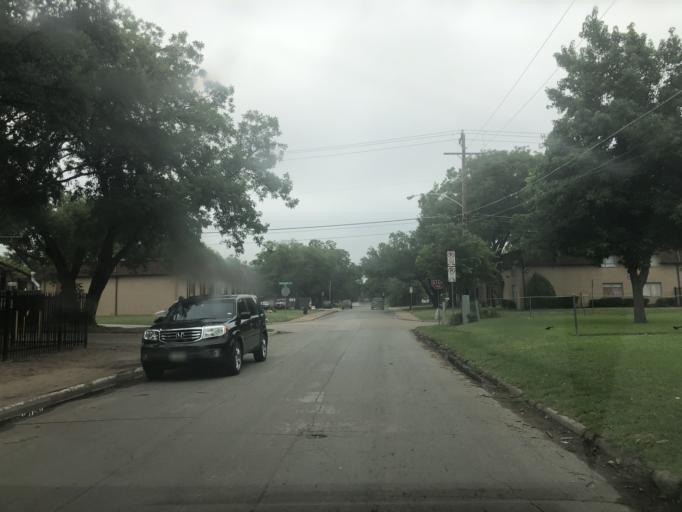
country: US
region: Texas
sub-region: Dallas County
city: Farmers Branch
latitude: 32.8608
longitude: -96.8746
